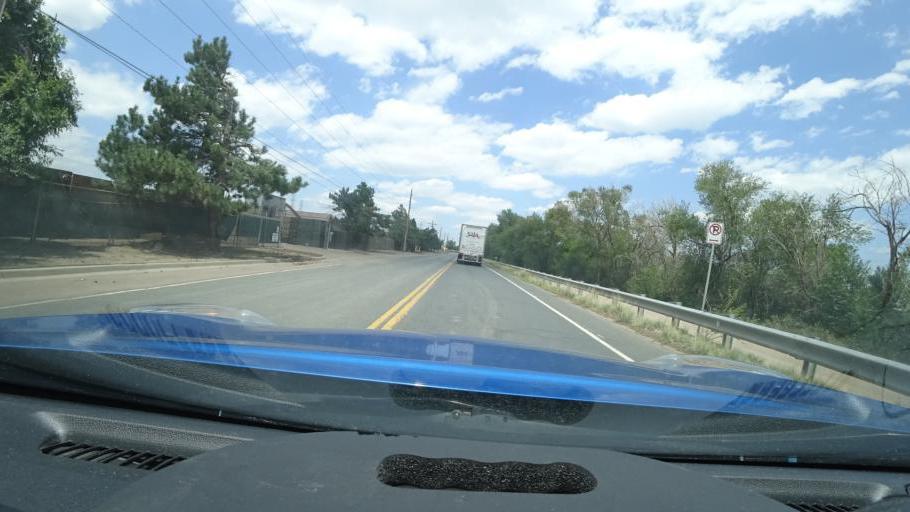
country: US
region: Colorado
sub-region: Arapahoe County
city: Englewood
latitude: 39.6623
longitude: -105.0049
